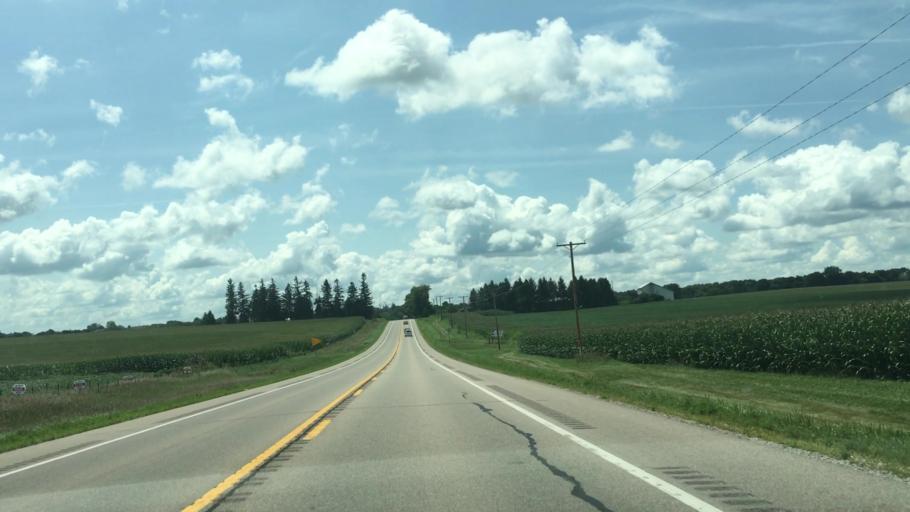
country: US
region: Iowa
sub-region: Johnson County
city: Solon
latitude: 41.8211
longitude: -91.4967
